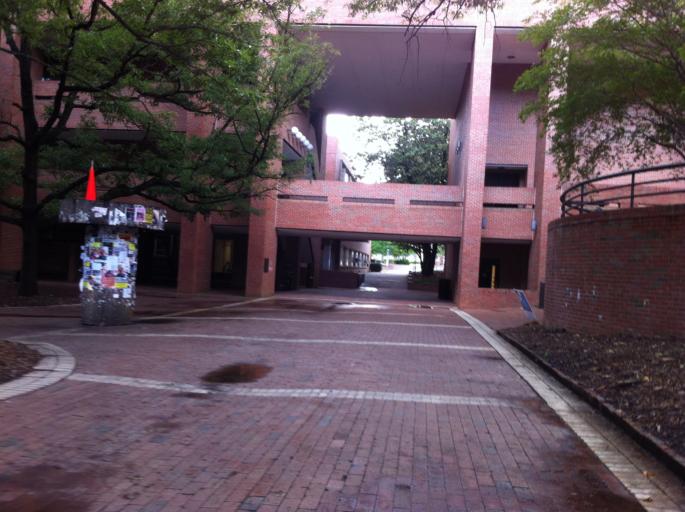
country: US
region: North Carolina
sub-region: Wake County
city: West Raleigh
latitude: 35.7876
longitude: -78.6713
